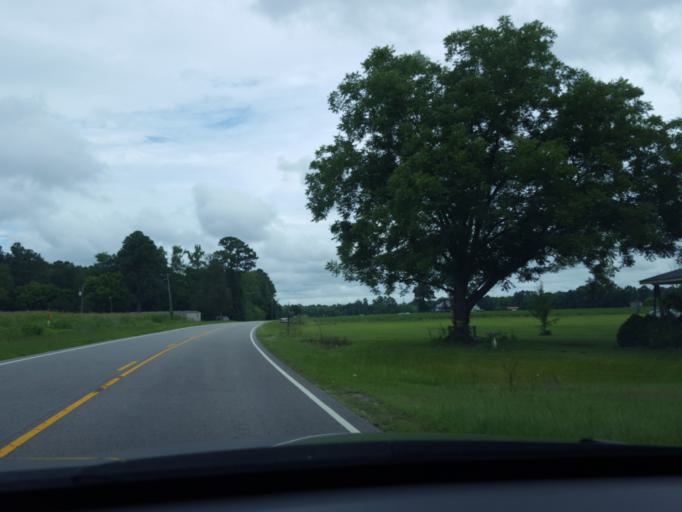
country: US
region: North Carolina
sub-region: Martin County
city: Williamston
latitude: 35.7113
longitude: -76.9864
